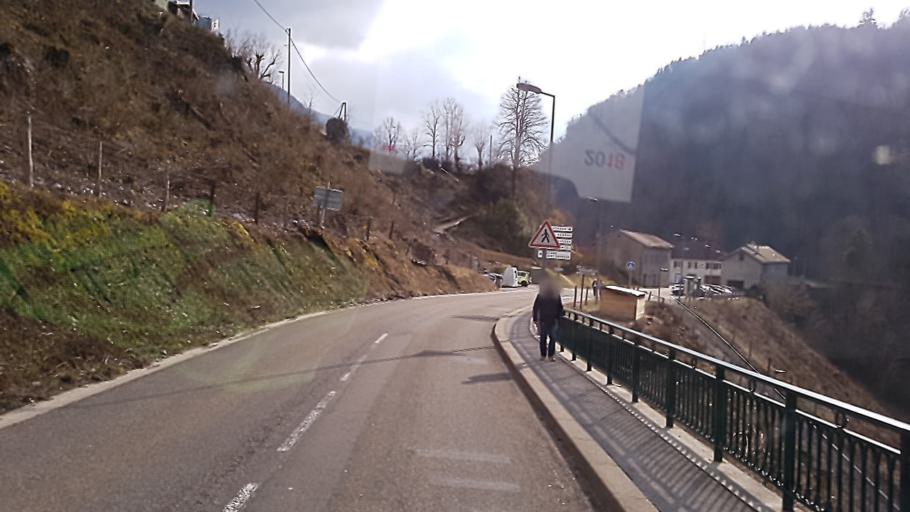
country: FR
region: Franche-Comte
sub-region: Departement du Jura
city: Saint-Claude
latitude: 46.3780
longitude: 5.8741
